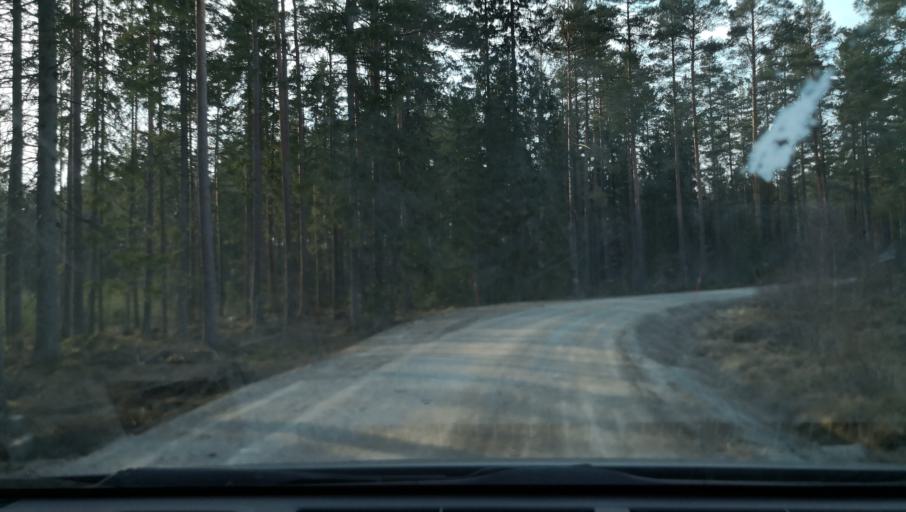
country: SE
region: OErebro
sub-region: Orebro Kommun
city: Hovsta
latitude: 59.3592
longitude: 15.3293
